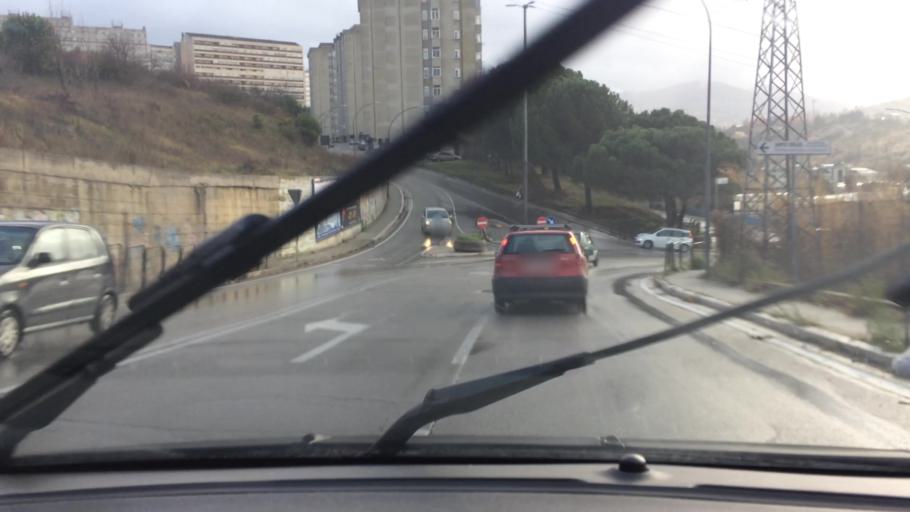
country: IT
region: Basilicate
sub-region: Provincia di Potenza
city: Potenza
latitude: 40.6363
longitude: 15.7873
